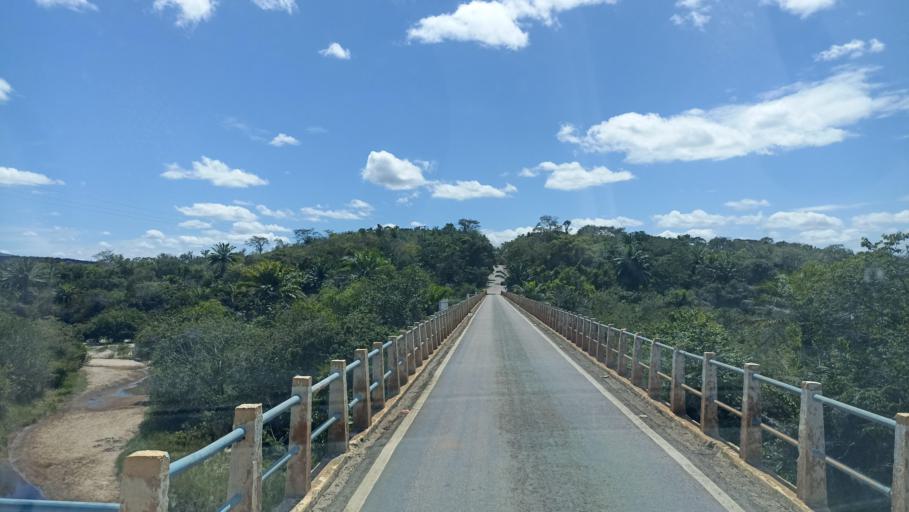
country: BR
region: Bahia
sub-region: Andarai
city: Vera Cruz
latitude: -12.7565
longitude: -41.3289
